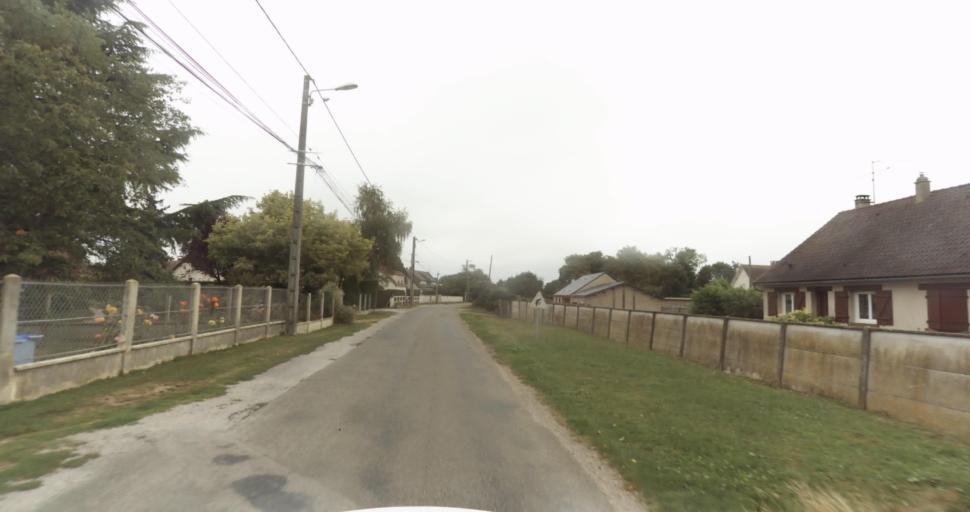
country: FR
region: Centre
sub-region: Departement d'Eure-et-Loir
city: Vert-en-Drouais
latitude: 48.7709
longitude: 1.2893
